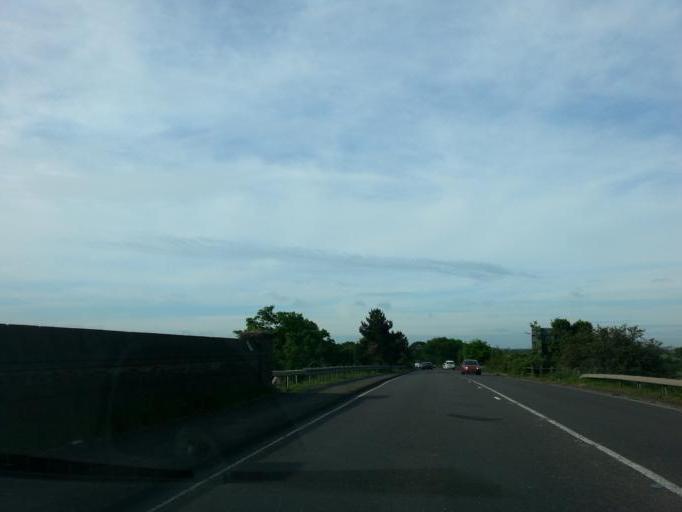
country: GB
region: England
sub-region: Nottinghamshire
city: Newark on Trent
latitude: 53.1180
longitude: -0.8186
